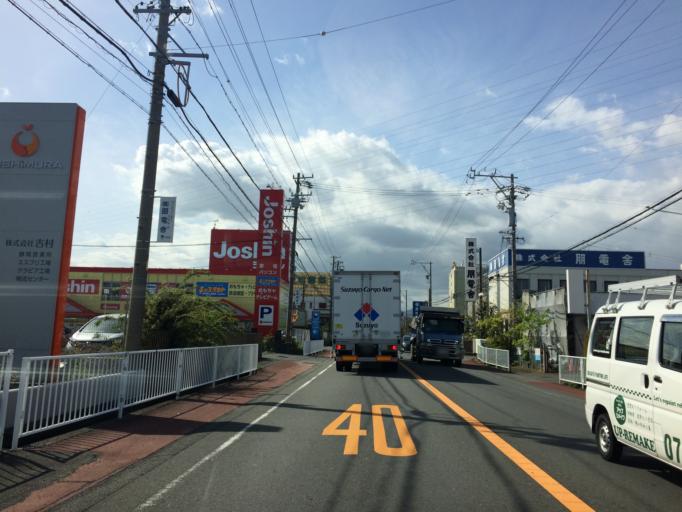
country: JP
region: Shizuoka
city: Yaizu
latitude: 34.8837
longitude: 138.2985
